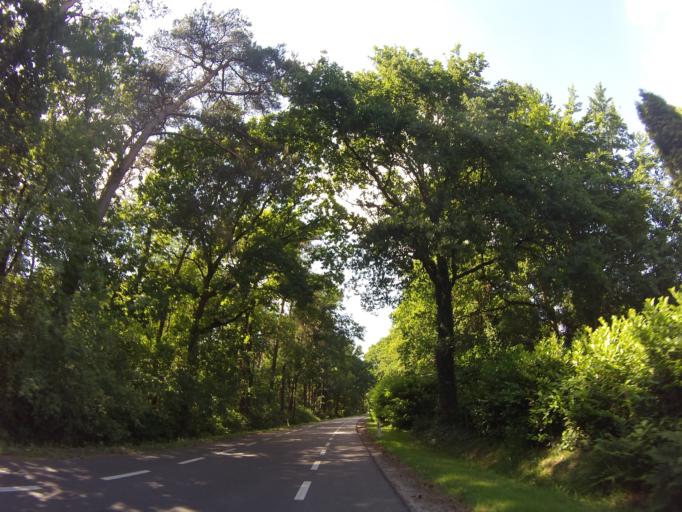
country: NL
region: Gelderland
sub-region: Gemeente Barneveld
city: Terschuur
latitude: 52.1532
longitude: 5.5255
